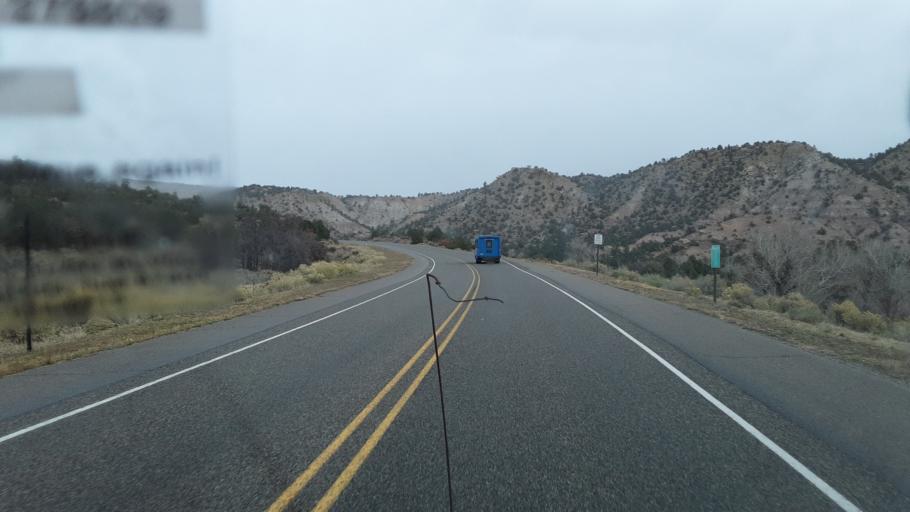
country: US
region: New Mexico
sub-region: Rio Arriba County
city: Santa Teresa
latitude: 36.3902
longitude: -106.4909
